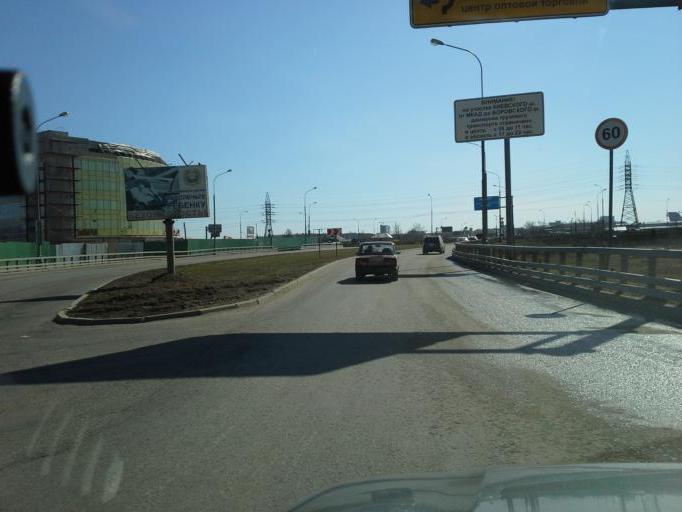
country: RU
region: Moskovskaya
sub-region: Leninskiy Rayon
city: Vnukovo
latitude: 55.6226
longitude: 37.2676
